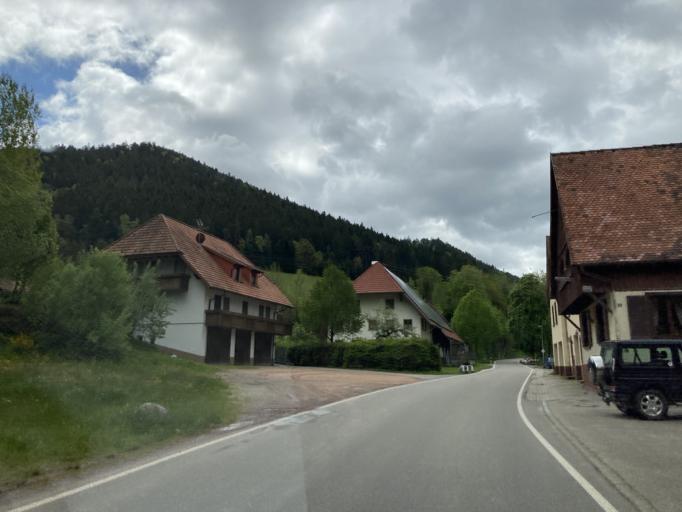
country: DE
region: Baden-Wuerttemberg
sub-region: Freiburg Region
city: Schonach im Schwarzwald
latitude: 48.2044
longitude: 8.1609
